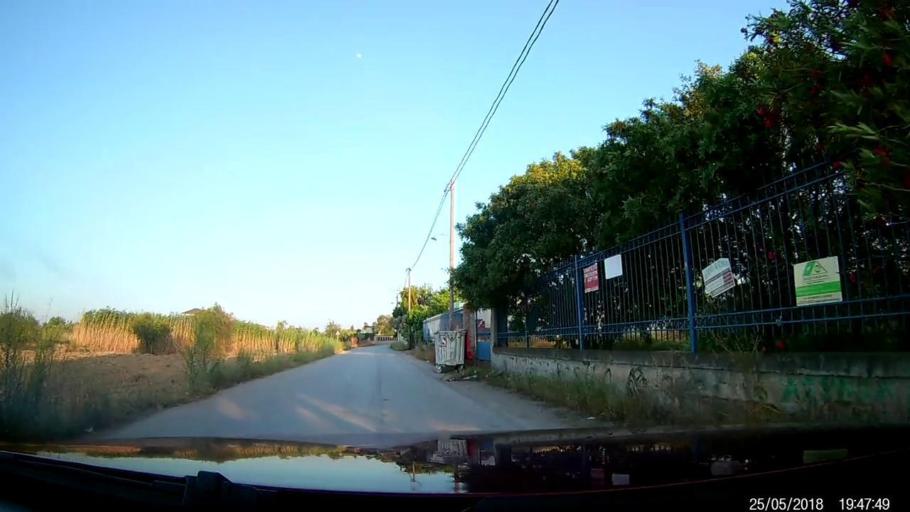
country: GR
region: Central Greece
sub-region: Nomos Evvoias
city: Ayios Nikolaos
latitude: 38.4204
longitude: 23.6365
